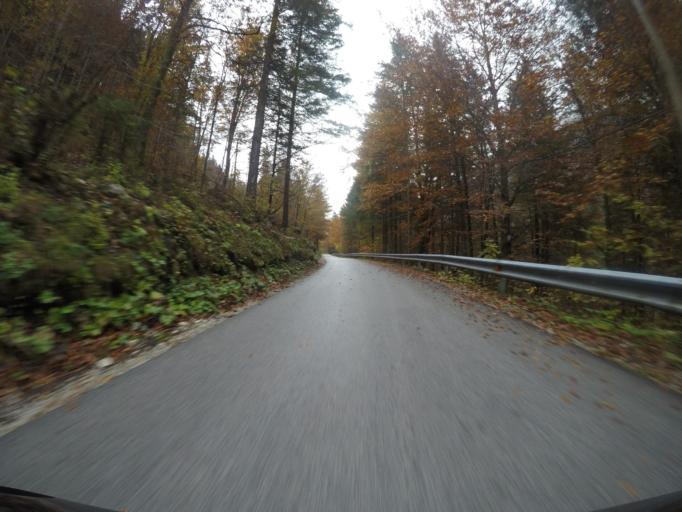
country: SI
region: Jesenice
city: Hrusica
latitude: 46.3967
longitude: 14.0036
